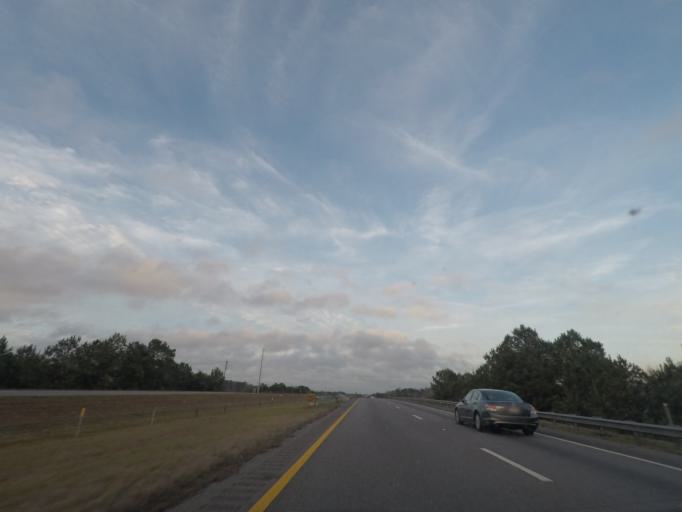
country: US
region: South Carolina
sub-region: Orangeburg County
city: Holly Hill
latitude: 33.3810
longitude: -80.5194
